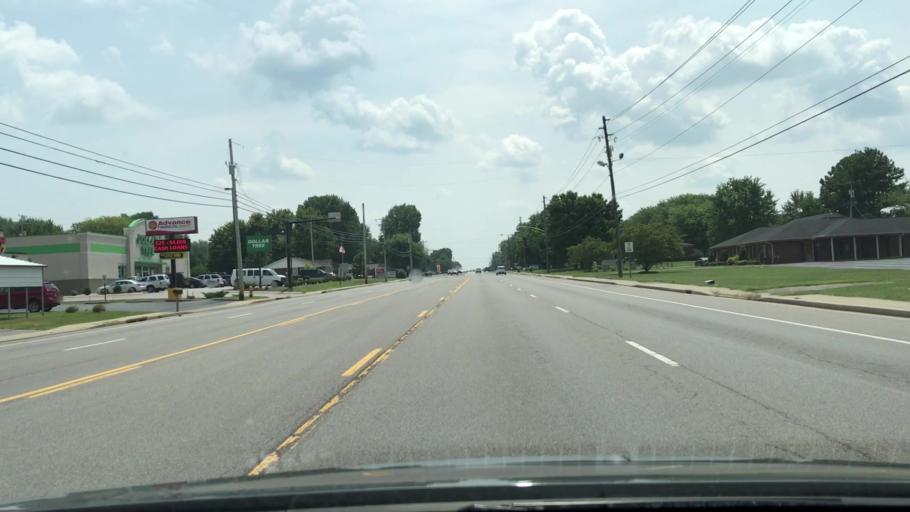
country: US
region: Tennessee
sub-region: Sumner County
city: Portland
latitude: 36.5685
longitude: -86.5119
